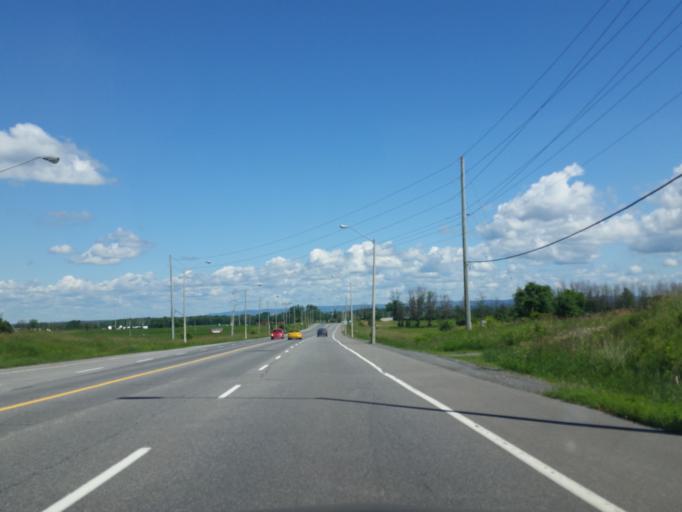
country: CA
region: Ontario
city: Bells Corners
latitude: 45.3295
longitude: -75.8374
